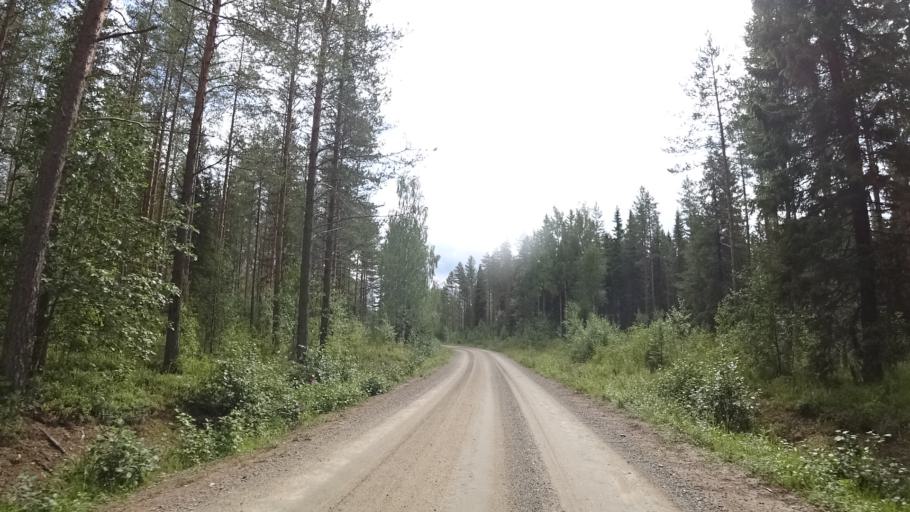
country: FI
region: North Karelia
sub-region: Joensuu
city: Ilomantsi
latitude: 62.9239
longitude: 31.3337
